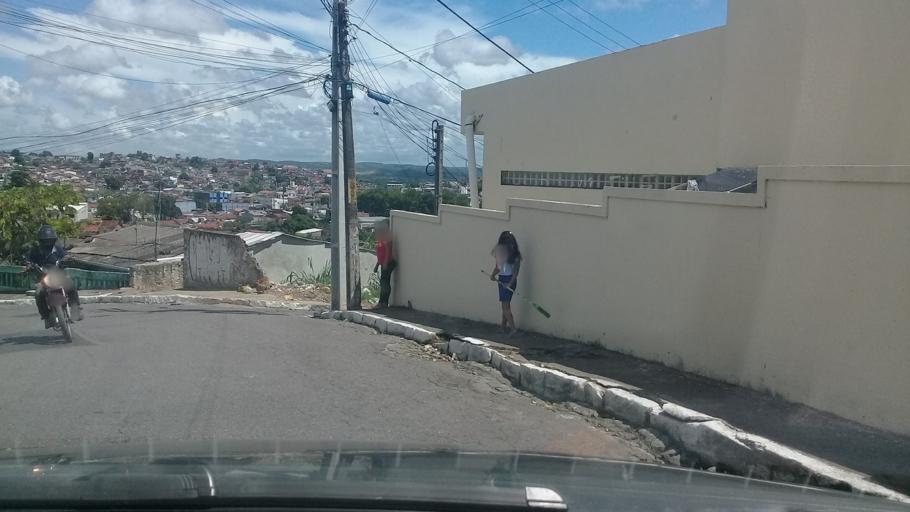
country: BR
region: Pernambuco
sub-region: Jaboatao Dos Guararapes
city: Jaboatao dos Guararapes
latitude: -8.1275
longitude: -34.9471
